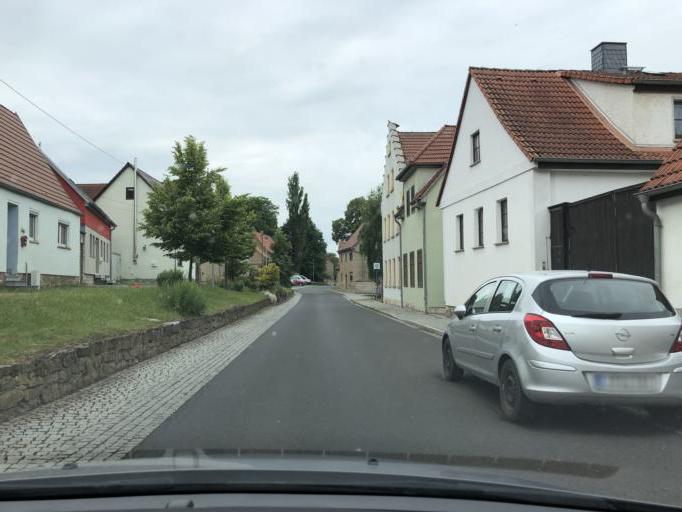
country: DE
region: Thuringia
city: Kromsdorf
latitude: 51.0023
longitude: 11.3877
